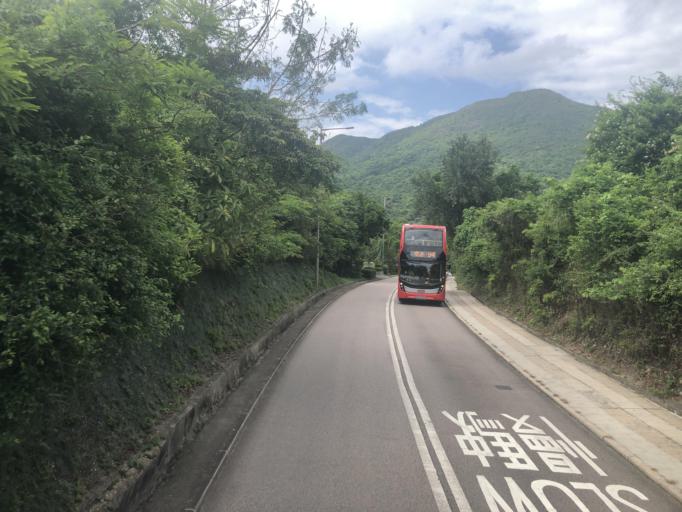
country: HK
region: Sai Kung
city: Sai Kung
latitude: 22.3891
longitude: 114.3075
